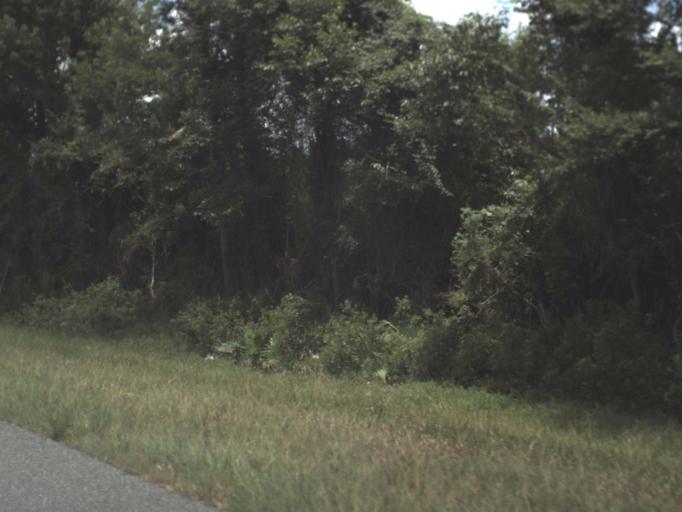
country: US
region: Florida
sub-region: Taylor County
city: Perry
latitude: 30.1429
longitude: -83.8485
